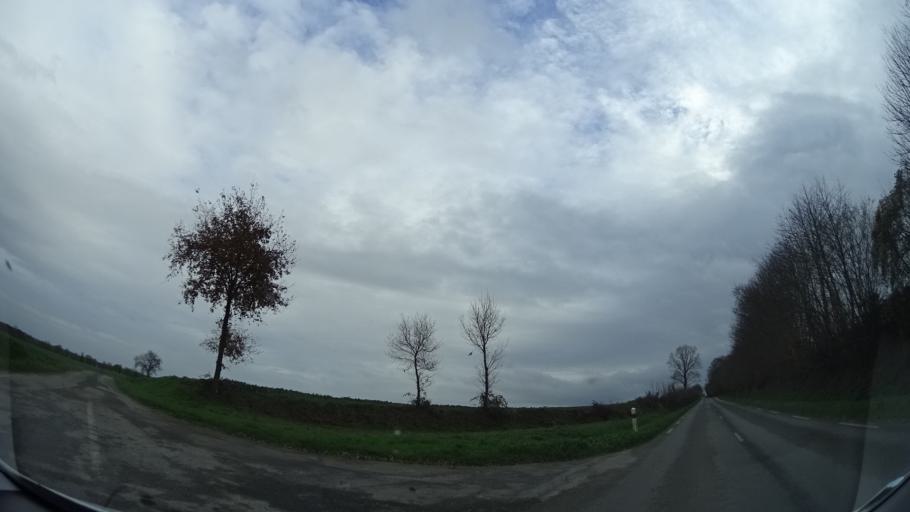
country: FR
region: Brittany
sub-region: Departement des Cotes-d'Armor
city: Evran
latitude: 48.3358
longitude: -1.9627
